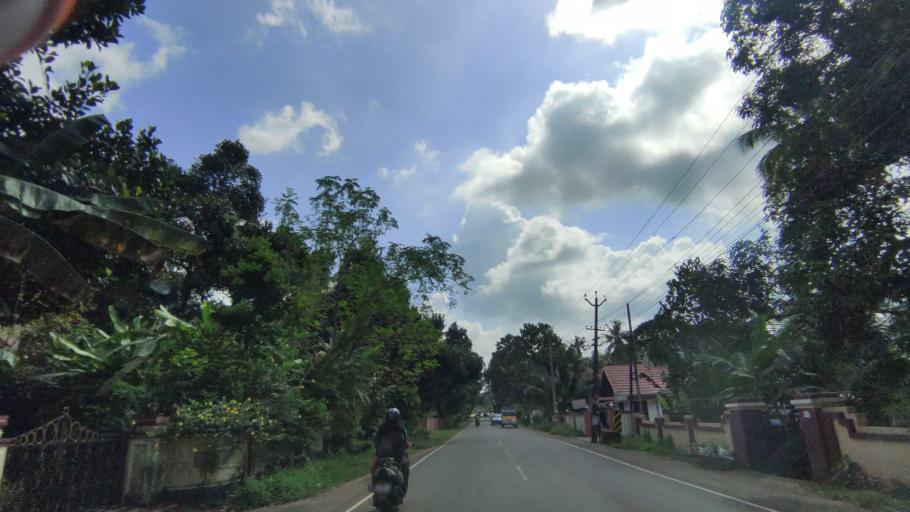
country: IN
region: Kerala
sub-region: Kottayam
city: Kottayam
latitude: 9.6746
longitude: 76.5348
